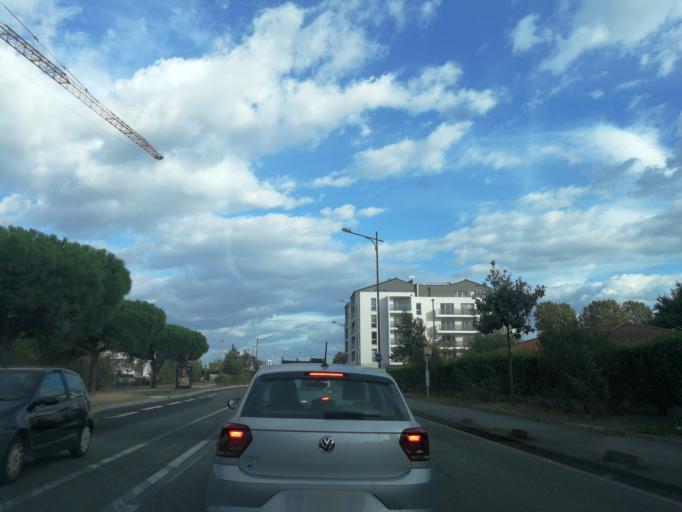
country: FR
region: Midi-Pyrenees
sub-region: Departement de la Haute-Garonne
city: L'Union
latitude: 43.6425
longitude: 1.4654
